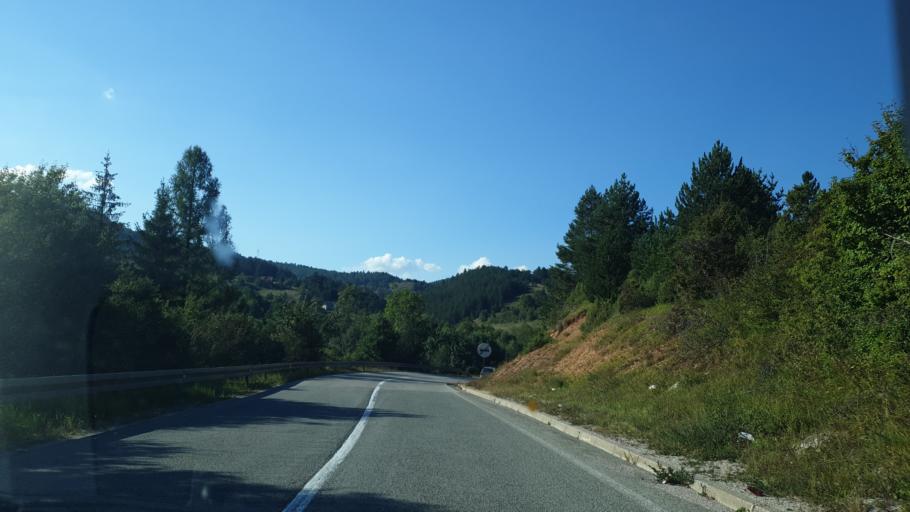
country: RS
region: Central Serbia
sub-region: Zlatiborski Okrug
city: Nova Varos
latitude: 43.5474
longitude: 19.7824
